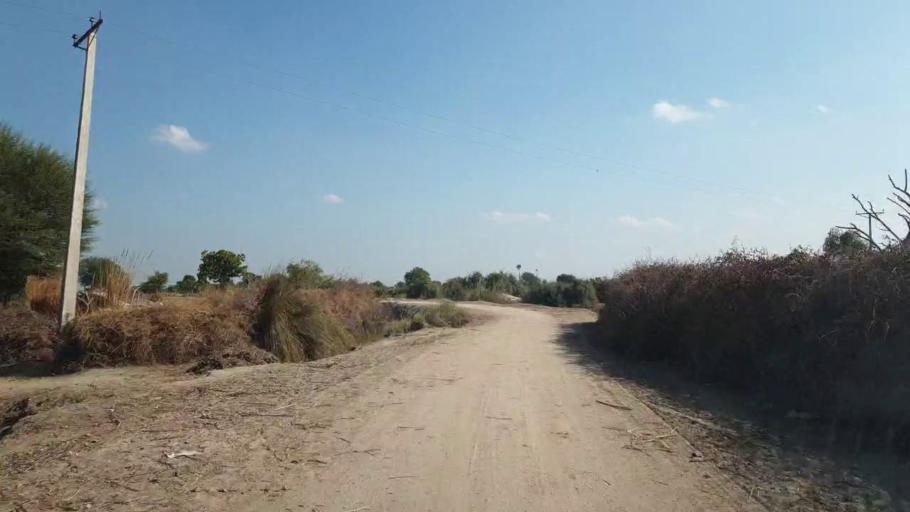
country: PK
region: Sindh
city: Shahpur Chakar
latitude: 26.0877
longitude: 68.5805
